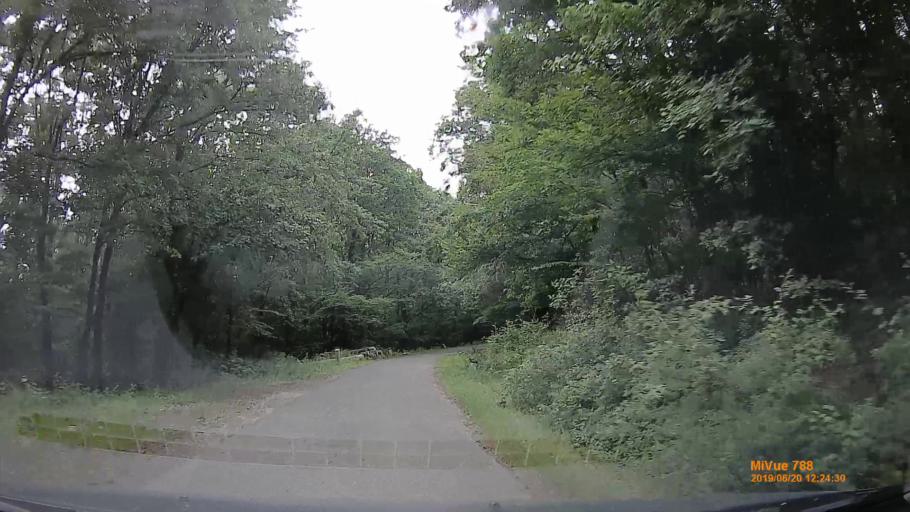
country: HU
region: Baranya
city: Hosszuheteny
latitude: 46.1916
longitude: 18.3427
